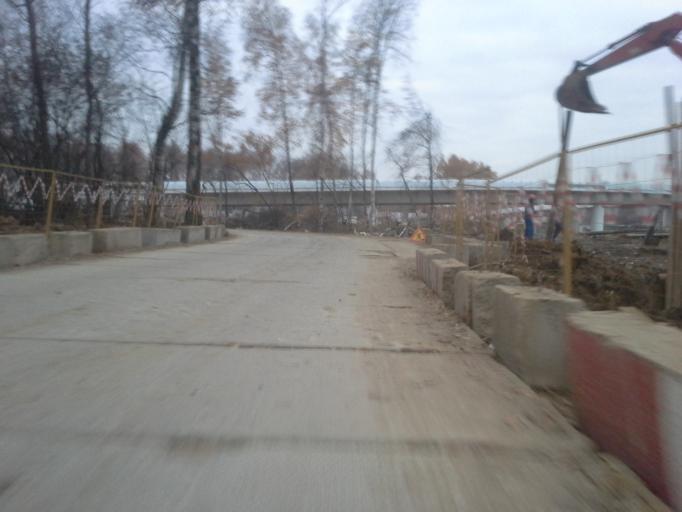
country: RU
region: Moskovskaya
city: Kommunarka
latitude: 55.5596
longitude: 37.4725
